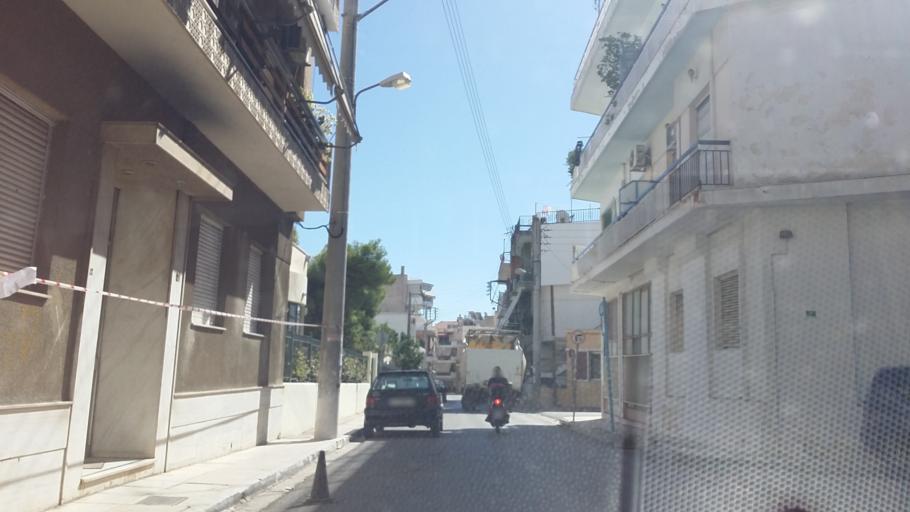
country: GR
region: Attica
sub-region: Nomarchia Athinas
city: Peristeri
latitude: 38.0261
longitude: 23.6898
